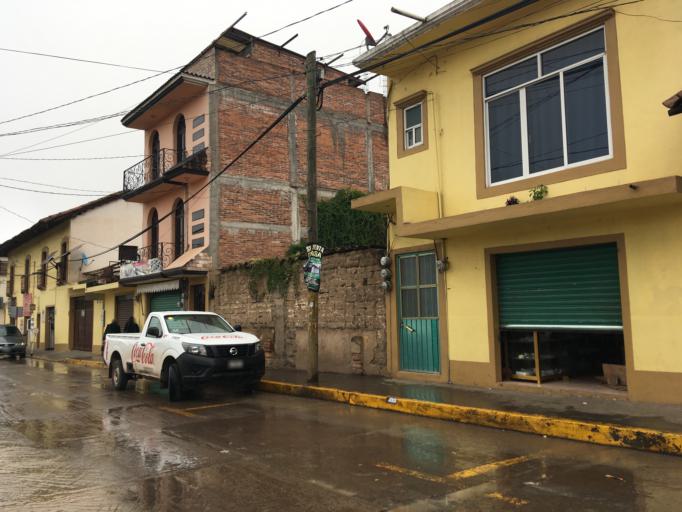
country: MX
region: Puebla
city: Chignahuapan
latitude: 19.8381
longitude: -98.0335
